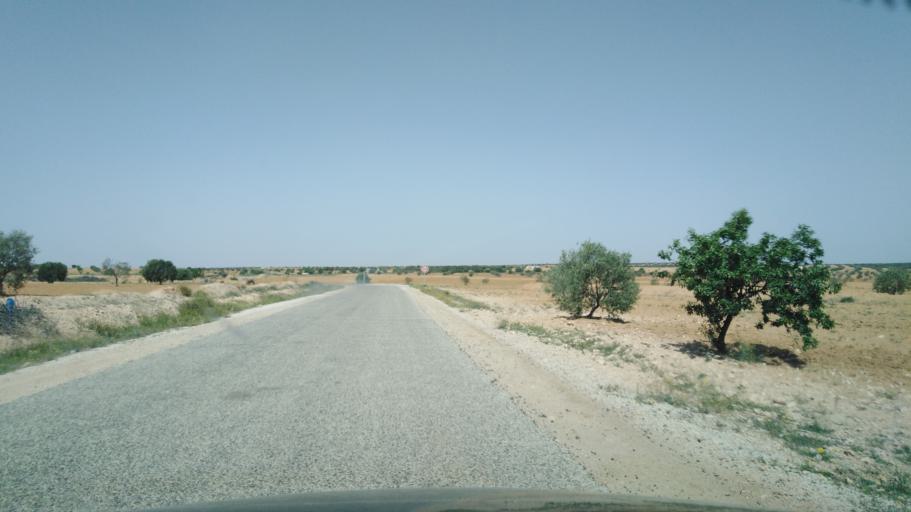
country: TN
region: Safaqis
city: Bi'r `Ali Bin Khalifah
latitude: 34.6782
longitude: 10.4164
